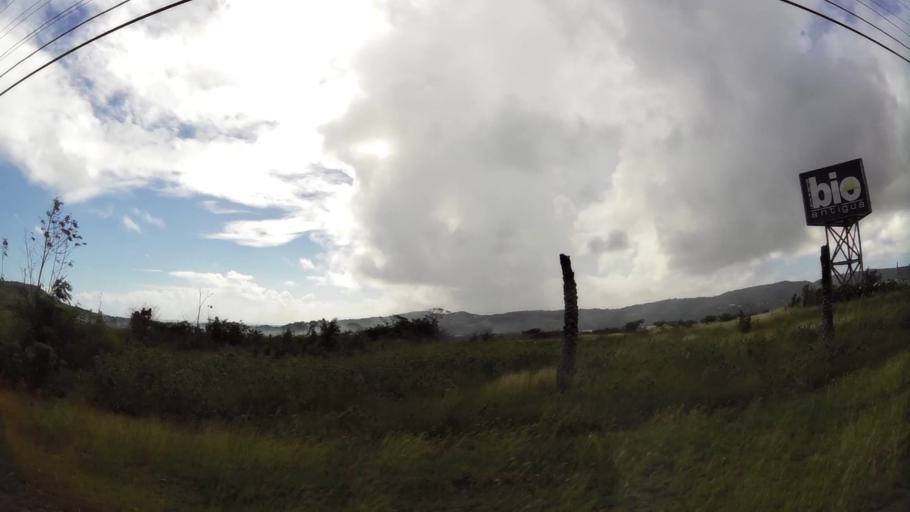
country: AG
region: Saint Paul
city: Liberta
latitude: 17.0537
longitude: -61.7438
